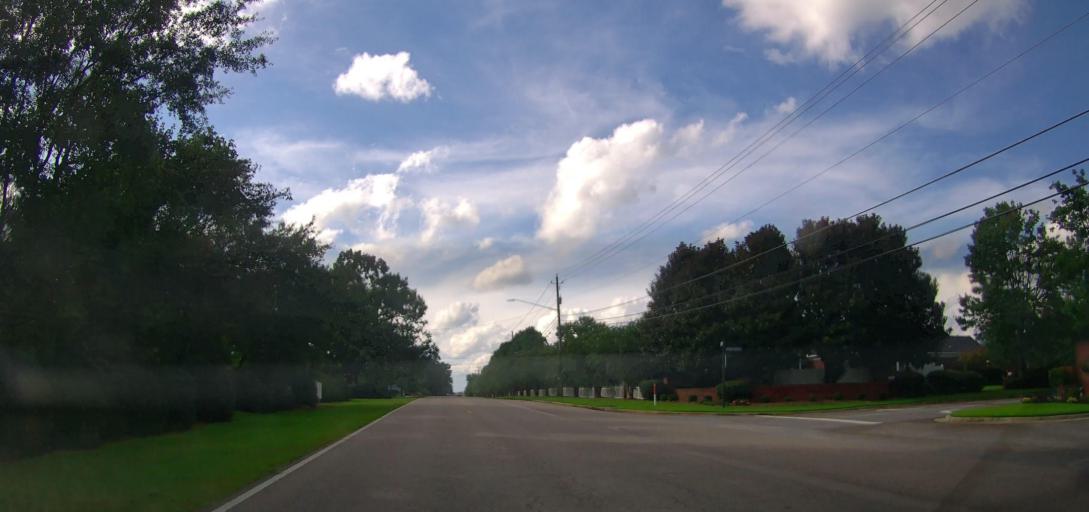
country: US
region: Alabama
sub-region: Russell County
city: Phenix City
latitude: 32.5129
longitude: -85.0222
